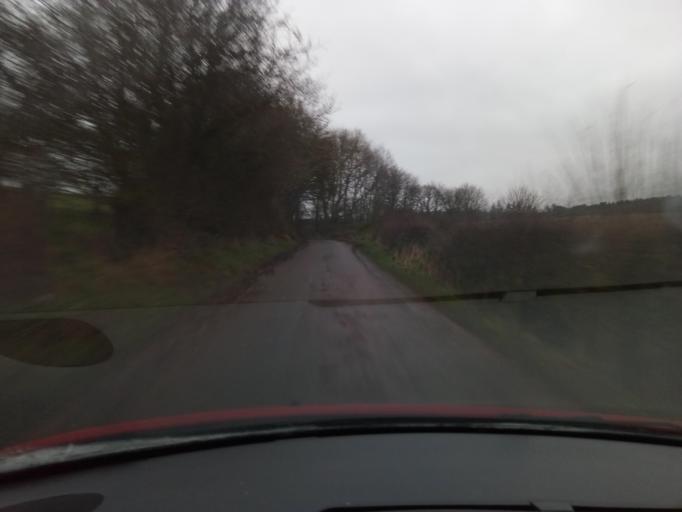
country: GB
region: Scotland
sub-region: The Scottish Borders
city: Kelso
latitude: 55.5445
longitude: -2.4356
